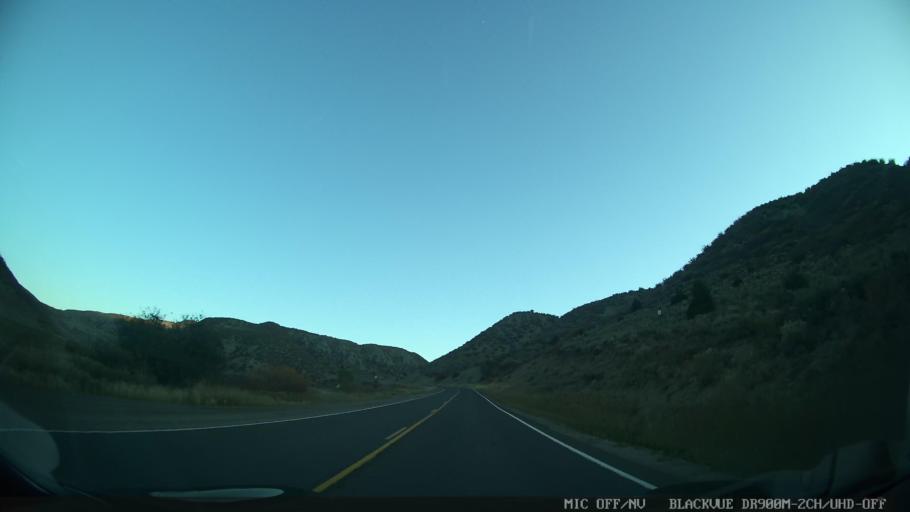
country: US
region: Colorado
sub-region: Eagle County
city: Edwards
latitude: 39.7953
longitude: -106.6798
